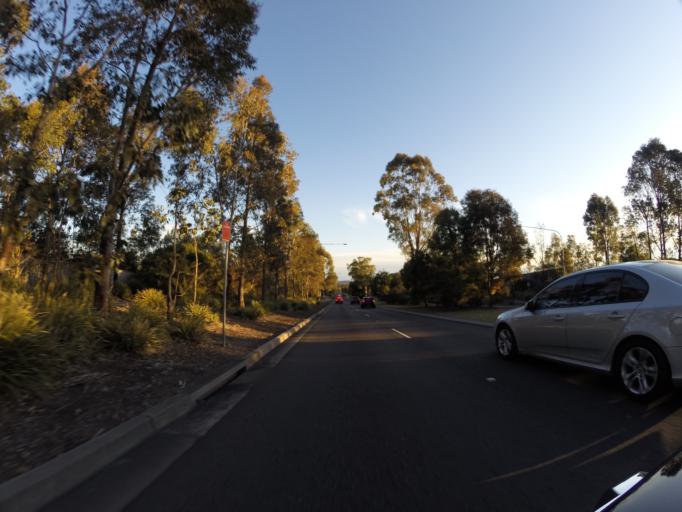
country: AU
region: New South Wales
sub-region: Fairfield
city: Cecil Park
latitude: -33.8900
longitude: 150.8603
